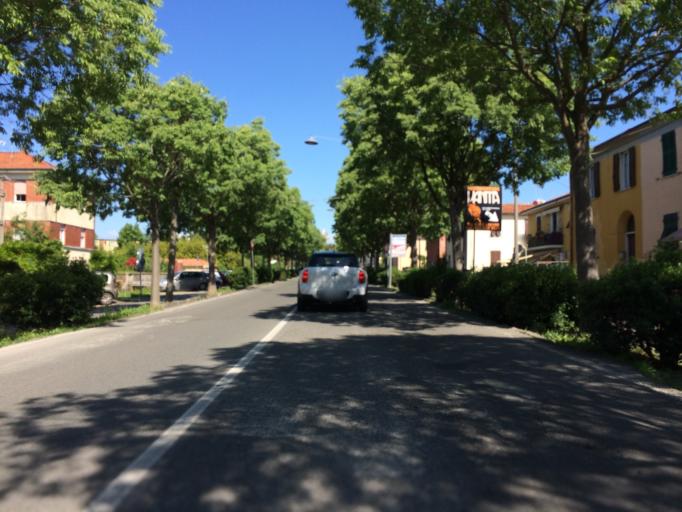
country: IT
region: Liguria
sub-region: Provincia di La Spezia
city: Sarzana
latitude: 44.1087
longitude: 9.9676
